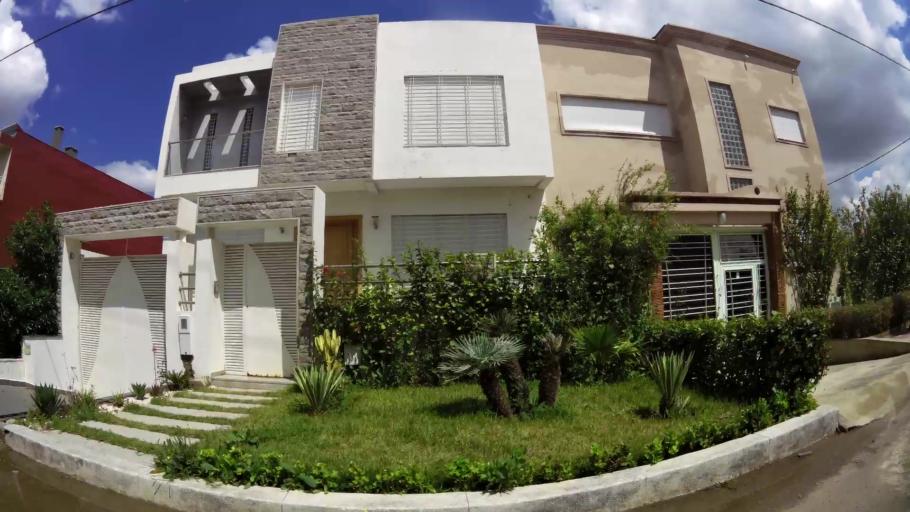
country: MA
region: Chaouia-Ouardigha
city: Nouaseur
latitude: 33.3950
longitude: -7.5627
